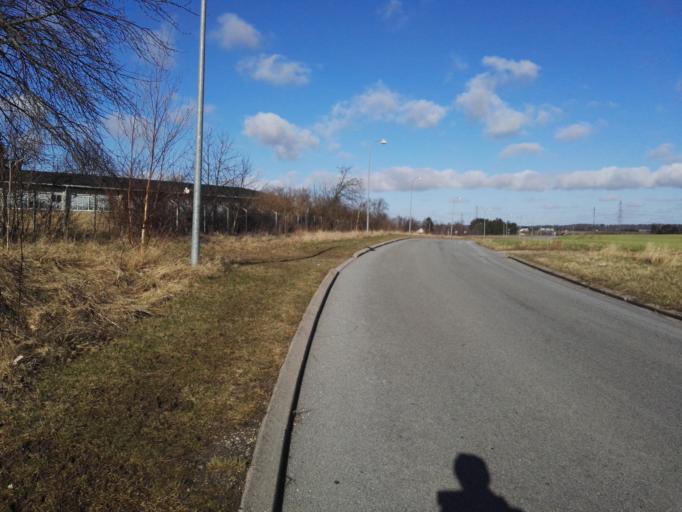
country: DK
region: Capital Region
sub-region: Egedal Kommune
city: Stenlose
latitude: 55.7871
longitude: 12.1809
